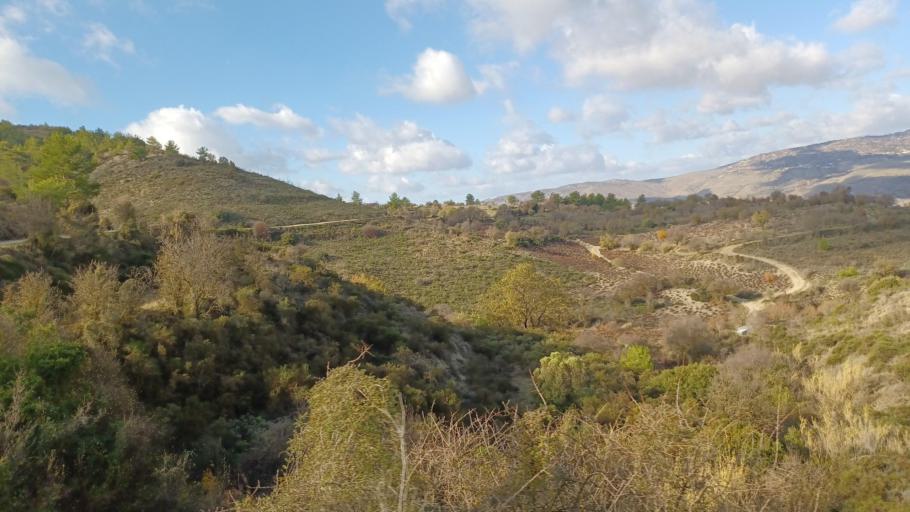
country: CY
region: Limassol
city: Pachna
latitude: 34.8553
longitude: 32.6908
